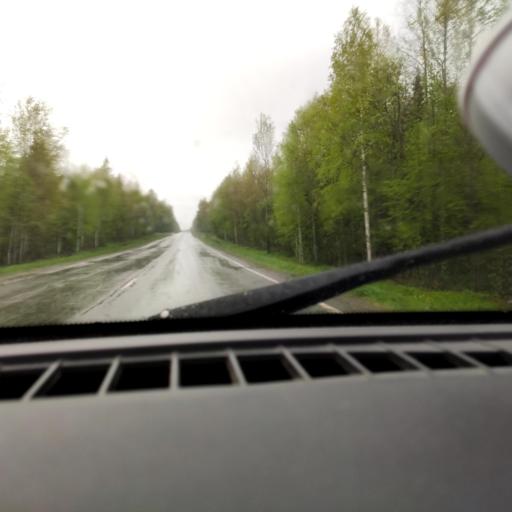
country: RU
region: Perm
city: Polazna
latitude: 58.2768
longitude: 56.1658
